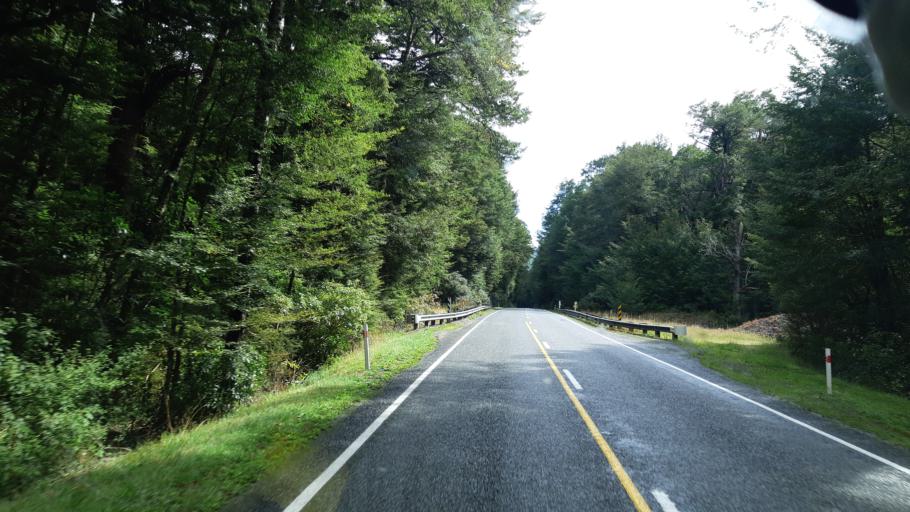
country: NZ
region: Canterbury
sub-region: Hurunui District
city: Amberley
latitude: -42.3807
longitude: 172.3129
